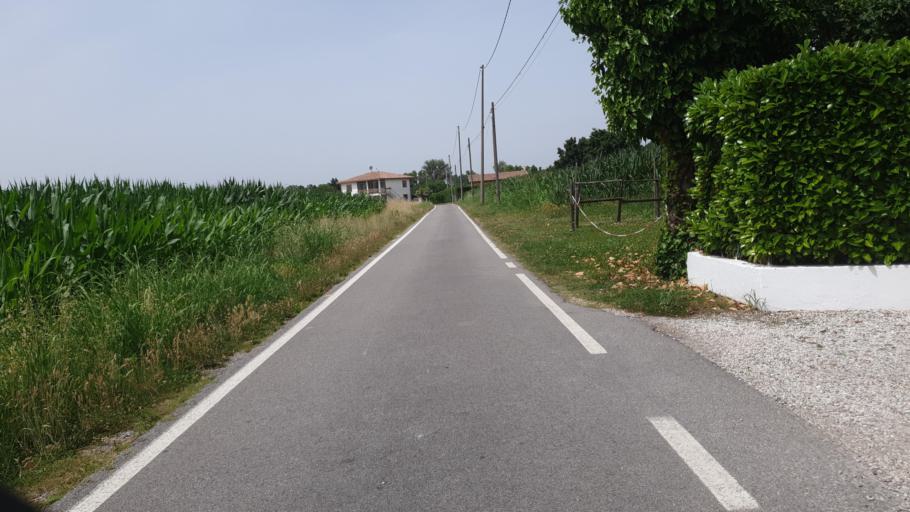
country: IT
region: Veneto
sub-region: Provincia di Padova
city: Polverara
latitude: 45.2950
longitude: 11.9516
